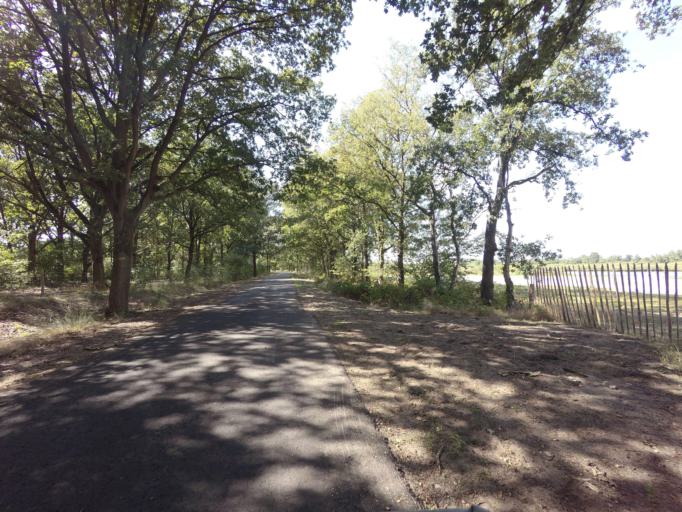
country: NL
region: North Brabant
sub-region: Gemeente Cranendonck
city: Cranendonck
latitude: 51.3009
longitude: 5.5514
